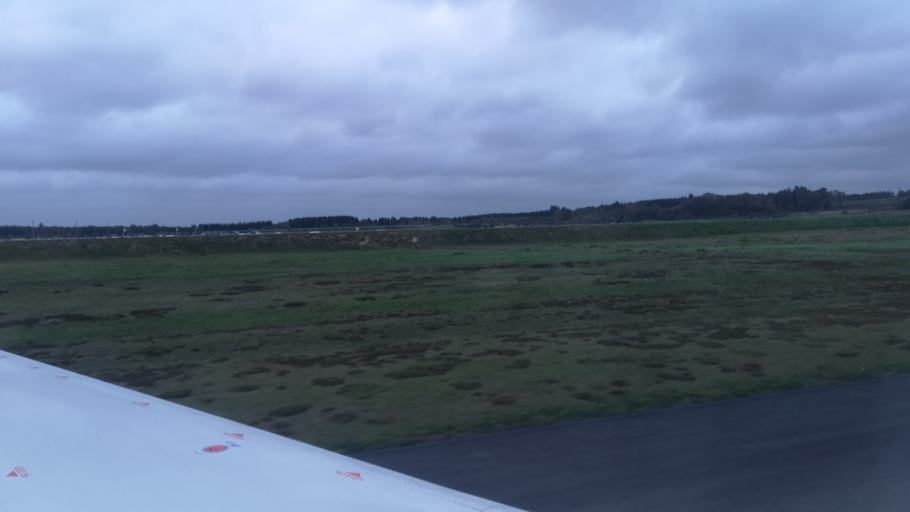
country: DK
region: South Denmark
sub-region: Billund Kommune
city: Billund
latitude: 55.7422
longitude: 9.1577
